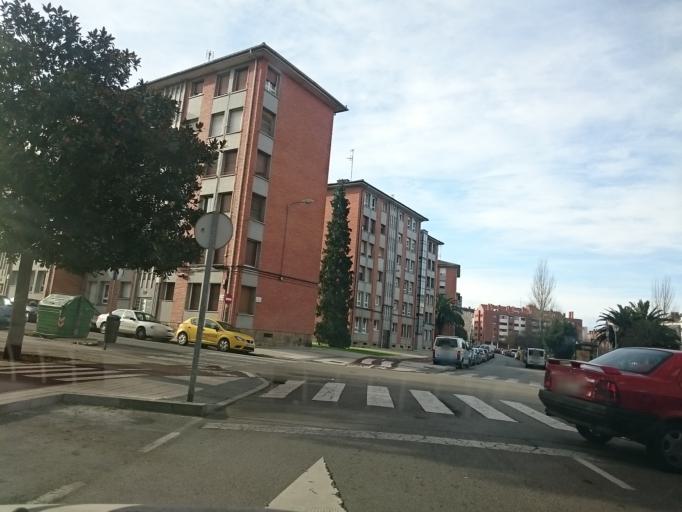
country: ES
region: Asturias
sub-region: Province of Asturias
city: Gijon
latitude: 43.5203
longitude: -5.6595
